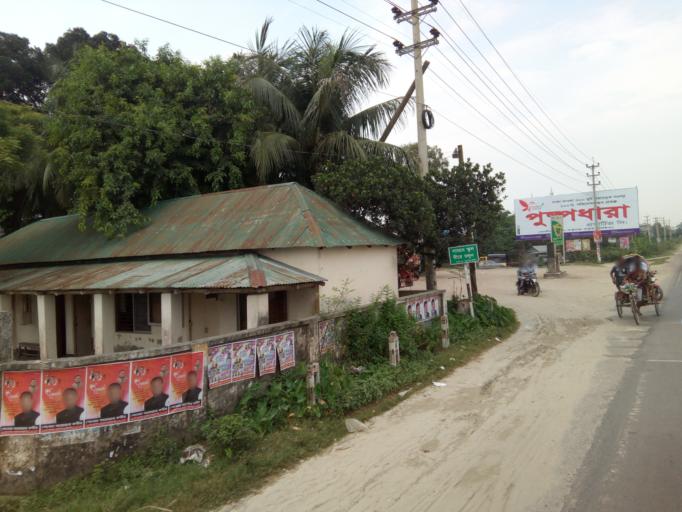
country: BD
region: Dhaka
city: Dohar
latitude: 23.5435
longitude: 90.2963
